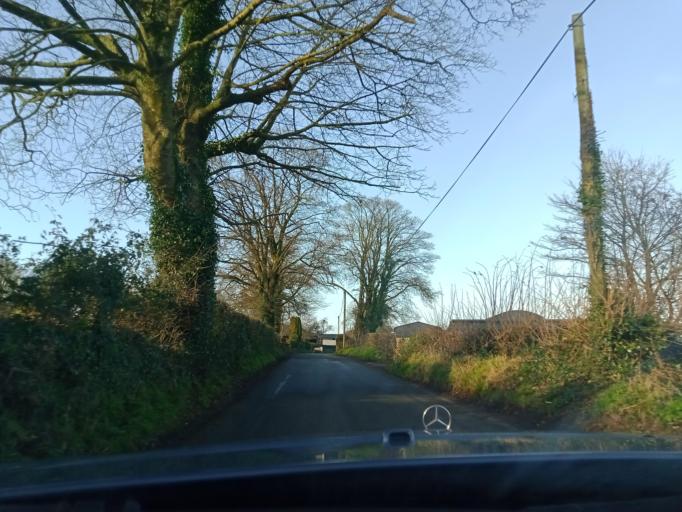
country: IE
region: Leinster
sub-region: Kilkenny
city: Callan
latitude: 52.4700
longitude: -7.4151
